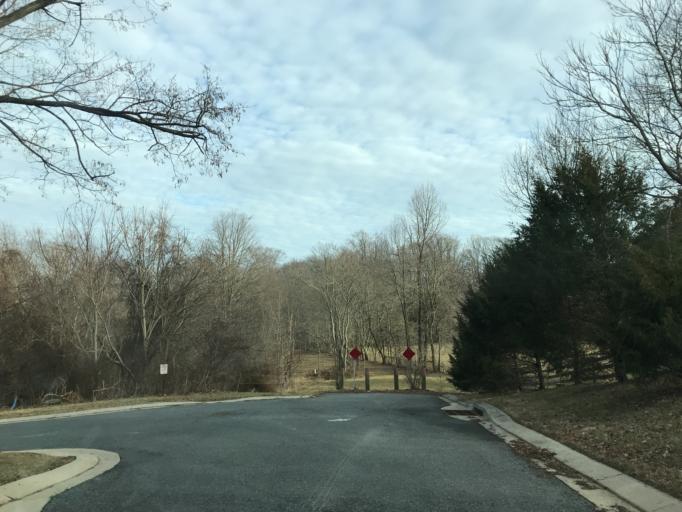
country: US
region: Maryland
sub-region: Baltimore County
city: Kingsville
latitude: 39.4378
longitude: -76.4171
